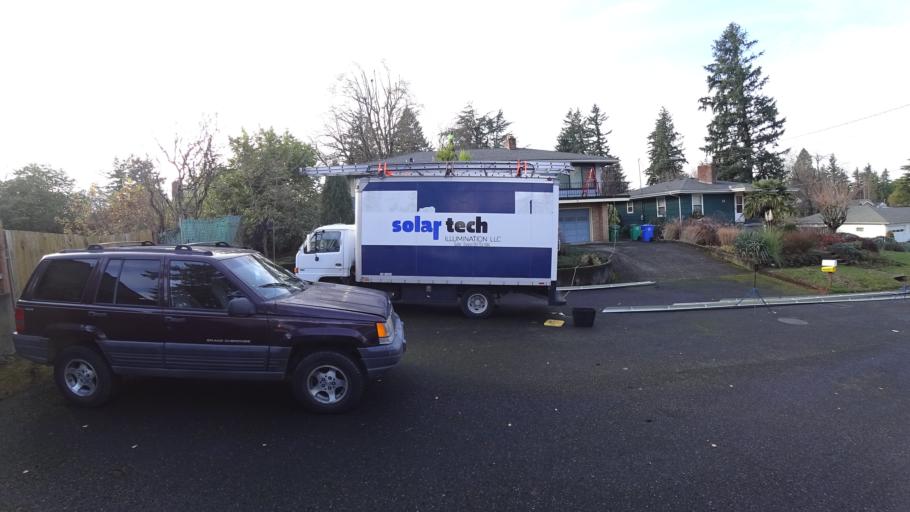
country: US
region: Oregon
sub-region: Multnomah County
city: Lents
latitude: 45.5229
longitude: -122.5279
